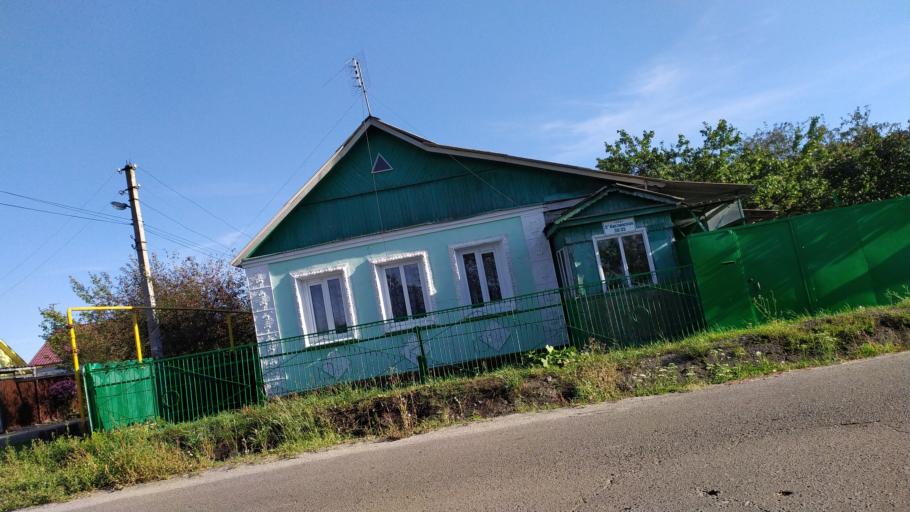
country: RU
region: Kursk
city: Kursk
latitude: 51.6445
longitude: 36.1451
